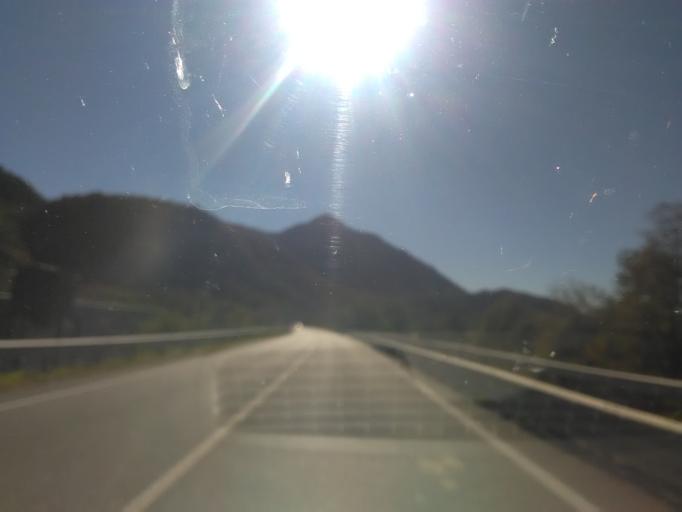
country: IT
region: Piedmont
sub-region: Provincia di Vercelli
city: Civiasco
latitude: 45.7887
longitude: 8.2728
